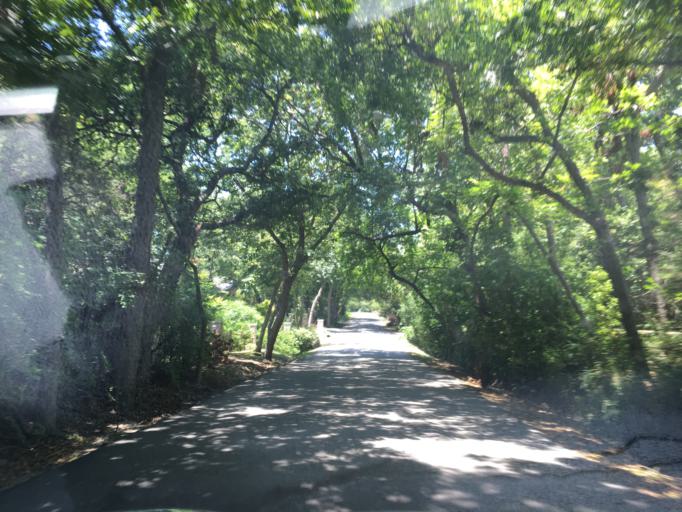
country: US
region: Texas
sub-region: Dallas County
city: Highland Park
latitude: 32.8414
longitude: -96.7357
